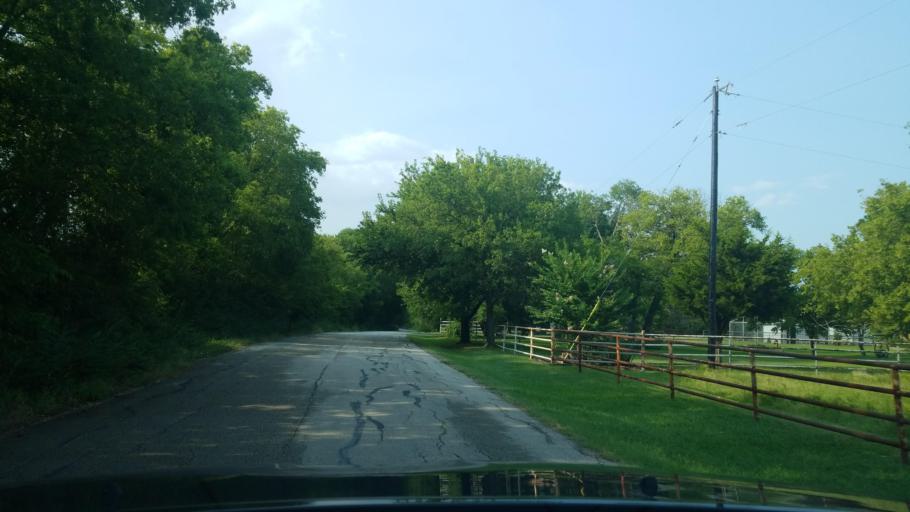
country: US
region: Texas
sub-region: Denton County
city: Cross Roads
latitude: 33.2533
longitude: -97.0613
